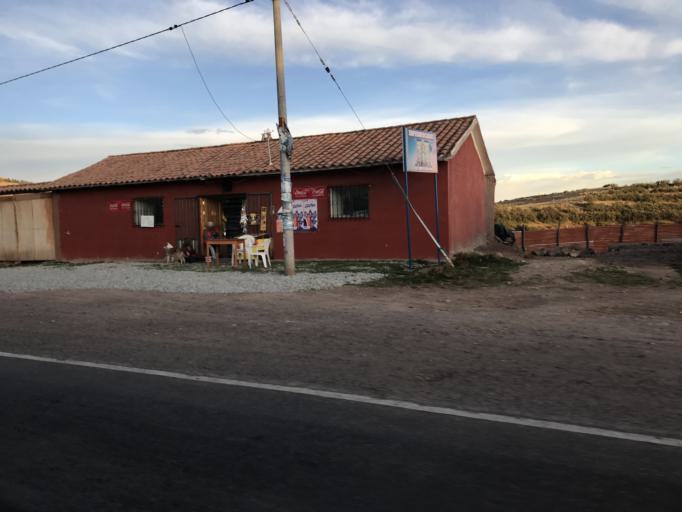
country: PE
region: Cusco
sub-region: Provincia de Cusco
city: Cusco
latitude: -13.4910
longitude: -71.9652
